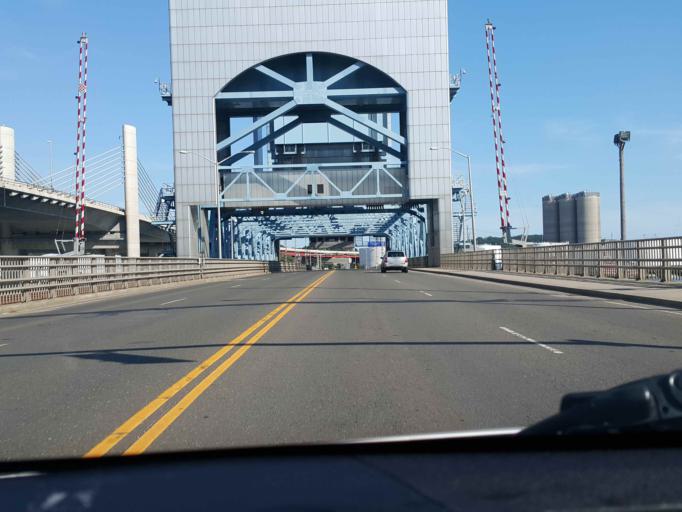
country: US
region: Connecticut
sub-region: New Haven County
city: New Haven
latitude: 41.2992
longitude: -72.9065
